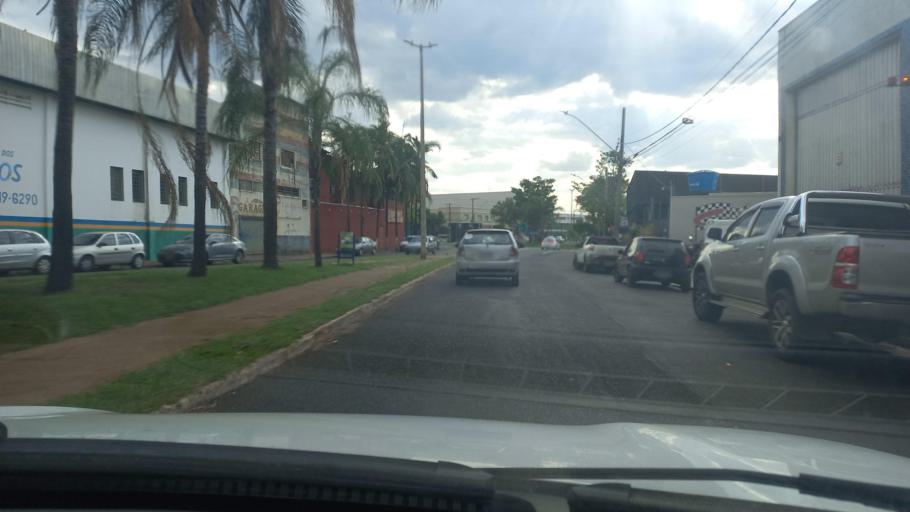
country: BR
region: Minas Gerais
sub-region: Uberaba
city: Uberaba
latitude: -19.7717
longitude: -47.9401
